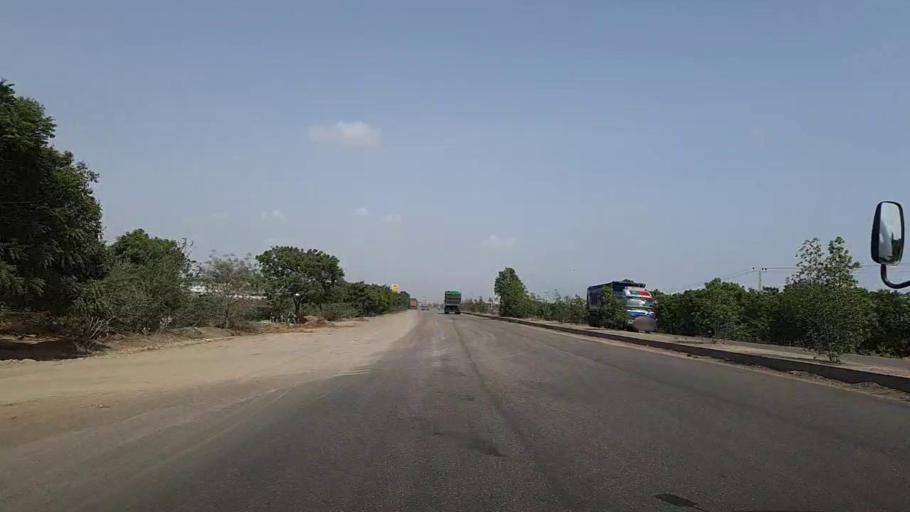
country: PK
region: Sindh
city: Malir Cantonment
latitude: 24.8652
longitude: 67.3866
